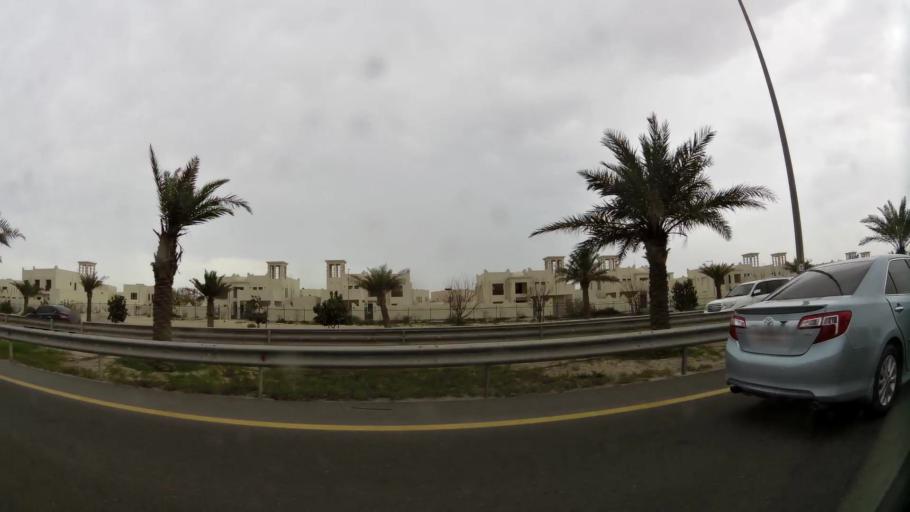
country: BH
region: Central Governorate
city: Madinat Hamad
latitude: 26.0905
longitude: 50.5392
